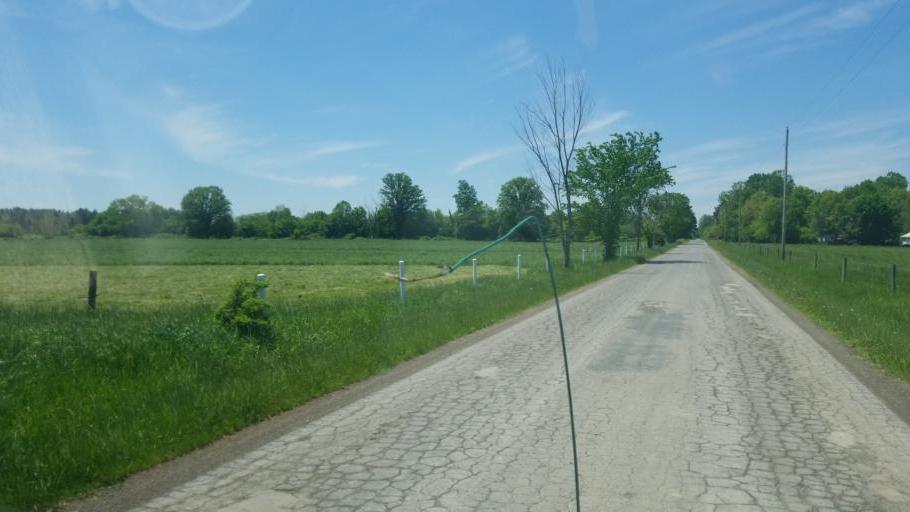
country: US
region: Ohio
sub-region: Huron County
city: Greenwich
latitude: 40.9679
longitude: -82.4196
